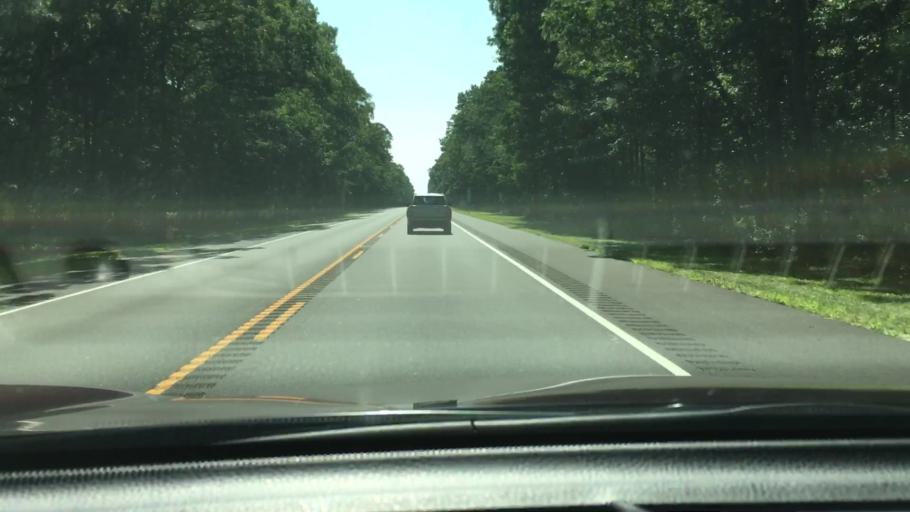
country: US
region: New Jersey
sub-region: Cumberland County
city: Laurel Lake
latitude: 39.3474
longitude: -74.9038
